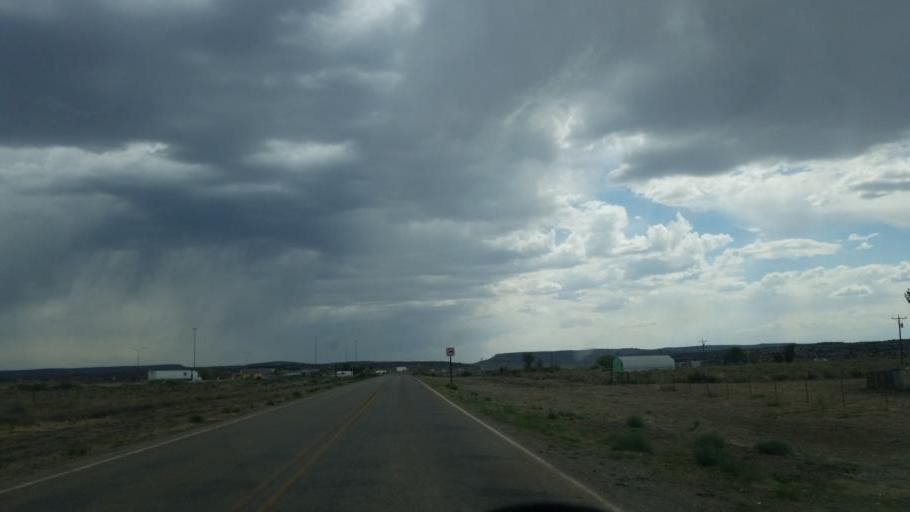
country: US
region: New Mexico
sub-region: McKinley County
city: Gallup
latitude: 35.4892
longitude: -108.8978
